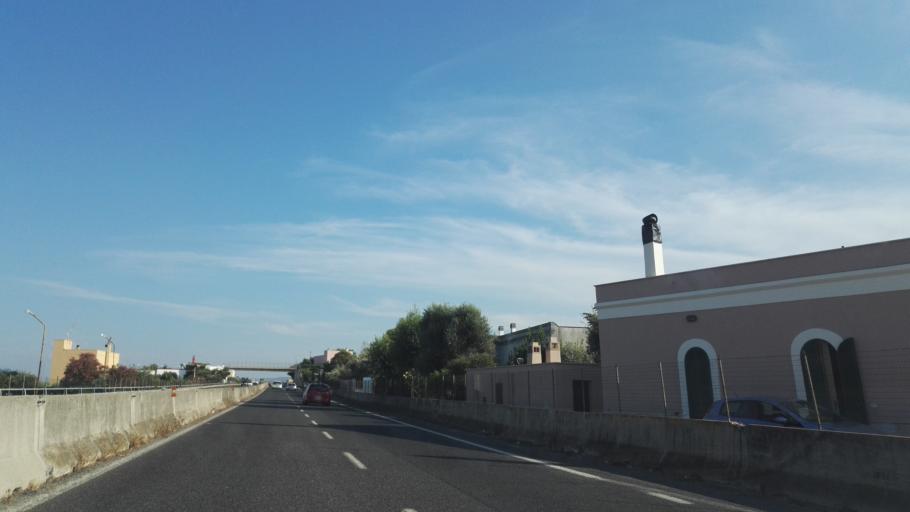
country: IT
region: Apulia
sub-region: Provincia di Brindisi
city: Fasano
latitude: 40.8931
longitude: 17.3315
